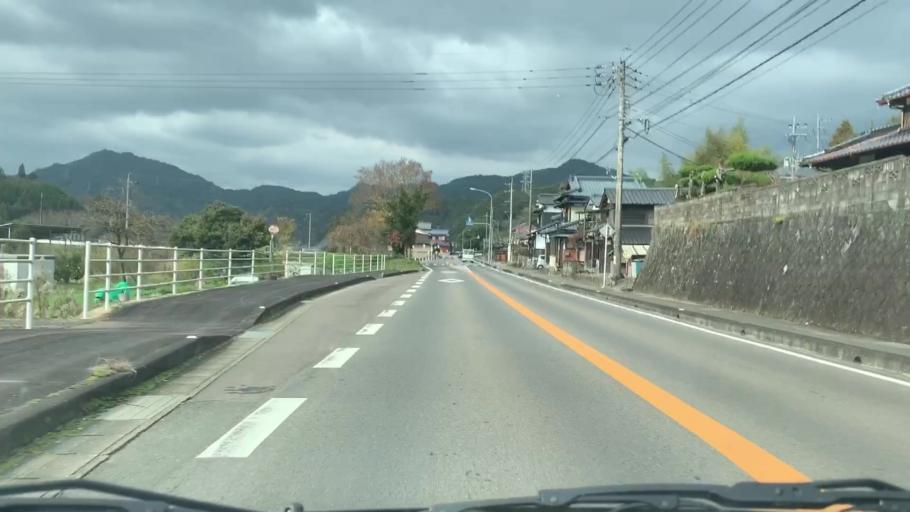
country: JP
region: Saga Prefecture
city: Ureshinomachi-shimojuku
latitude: 33.1301
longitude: 130.0328
